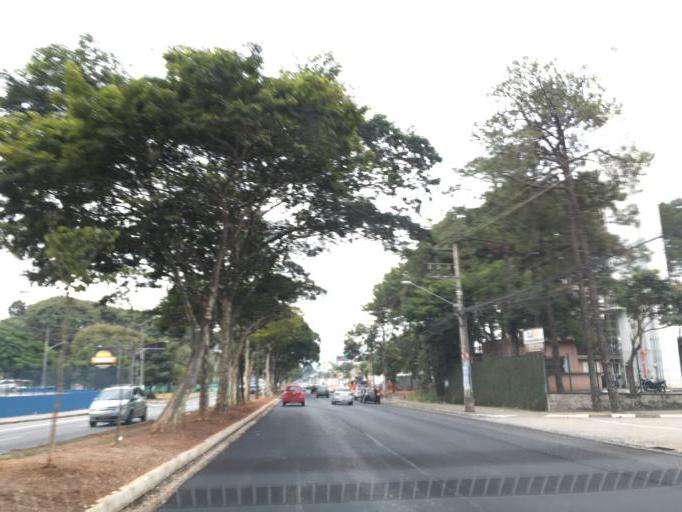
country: BR
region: Sao Paulo
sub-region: Osasco
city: Osasco
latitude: -23.5530
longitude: -46.7422
